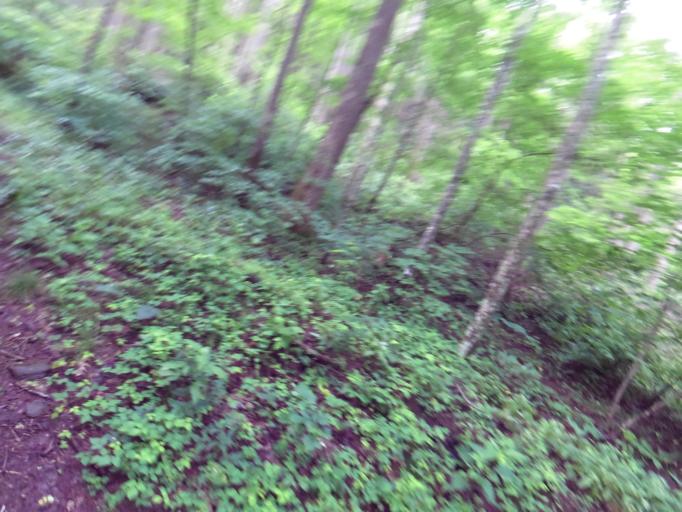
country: US
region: Tennessee
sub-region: Blount County
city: Wildwood
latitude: 35.5879
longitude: -83.7552
